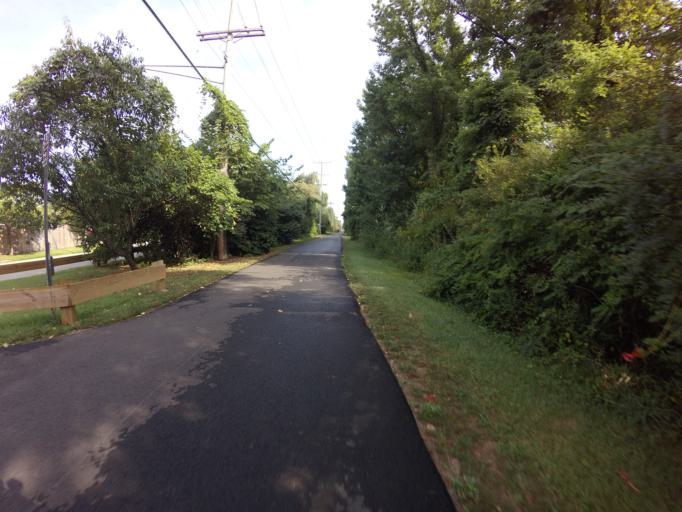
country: US
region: Maryland
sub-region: Anne Arundel County
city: Glen Burnie
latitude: 39.1461
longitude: -76.6139
